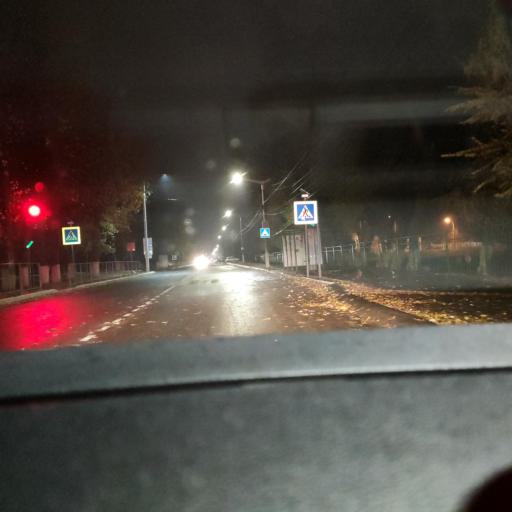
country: RU
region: Voronezj
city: Semiluki
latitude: 51.6952
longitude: 39.0311
